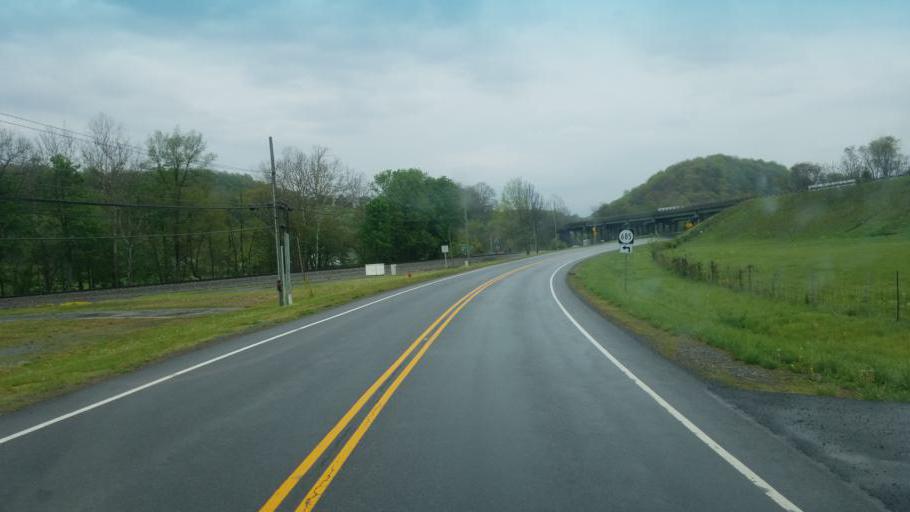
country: US
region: Virginia
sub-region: Smyth County
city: Atkins
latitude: 36.8735
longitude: -81.4008
